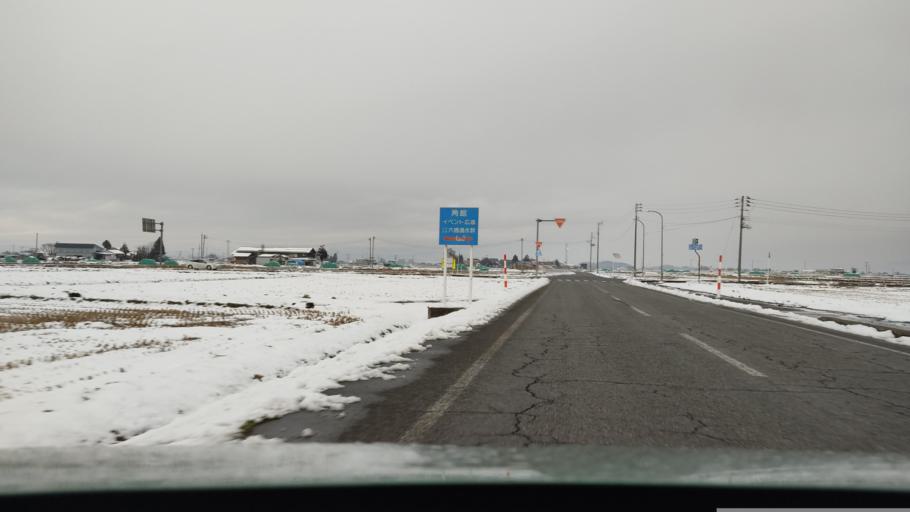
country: JP
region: Akita
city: Omagari
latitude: 39.4284
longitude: 140.5357
